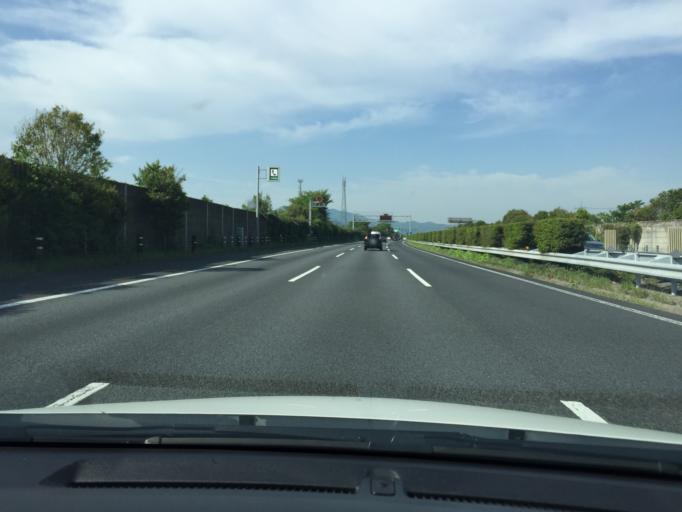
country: JP
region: Tochigi
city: Tochigi
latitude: 36.4068
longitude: 139.7142
